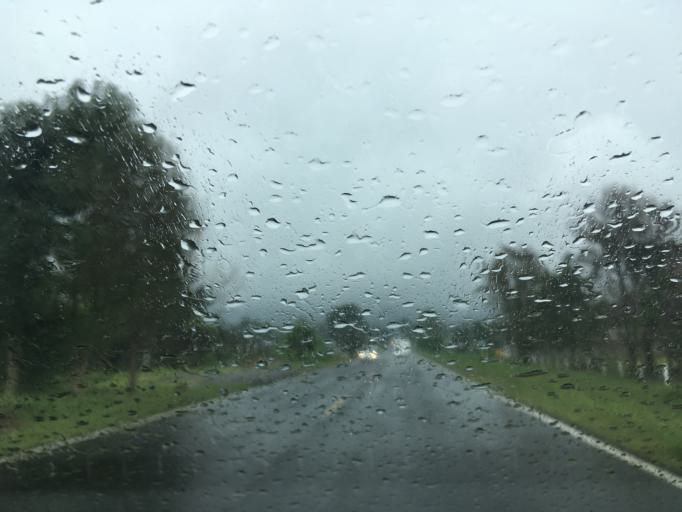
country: MX
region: Michoacan
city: Tingambato
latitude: 19.5010
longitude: -101.8683
